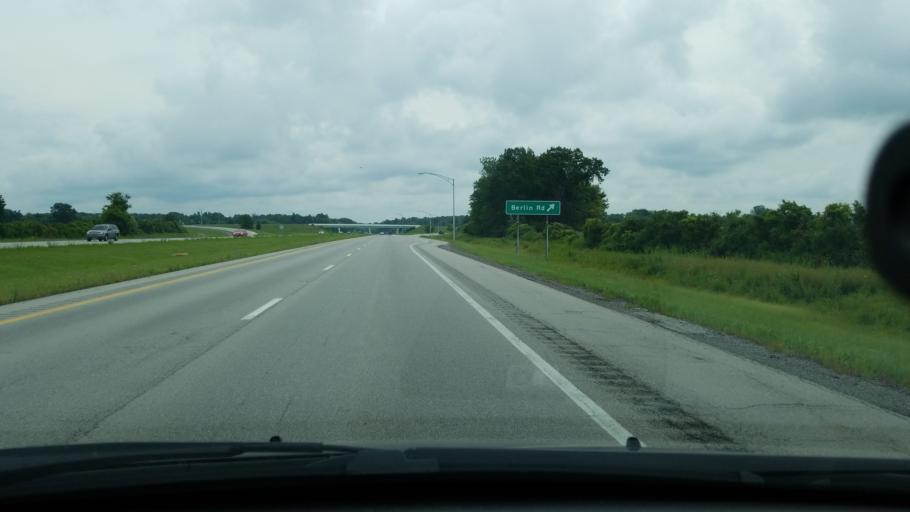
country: US
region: Ohio
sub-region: Erie County
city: Huron
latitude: 41.3685
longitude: -82.5275
